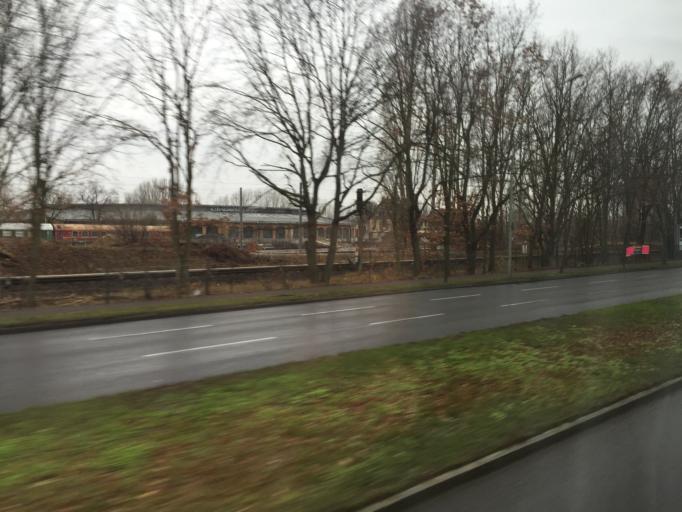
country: DE
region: Berlin
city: Niederschoneweide
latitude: 52.4476
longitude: 13.5236
